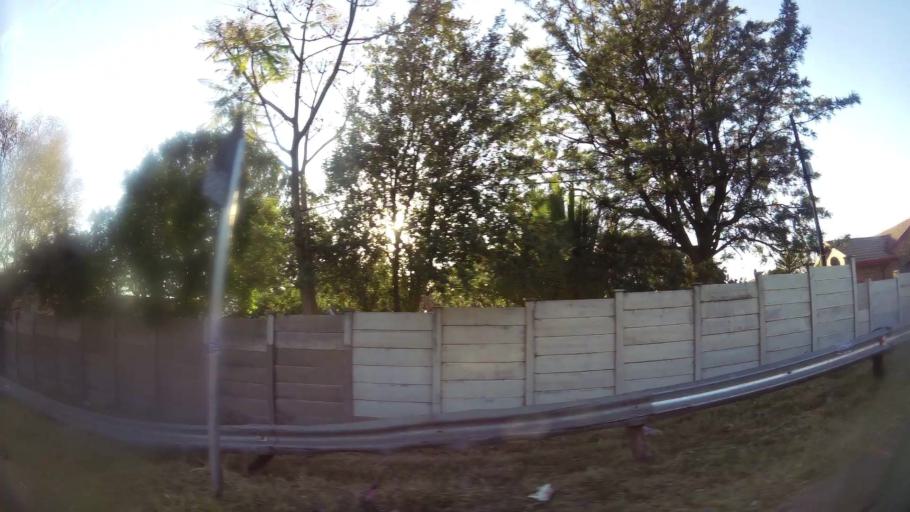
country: ZA
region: Gauteng
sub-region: City of Tshwane Metropolitan Municipality
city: Centurion
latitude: -25.9010
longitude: 28.1430
